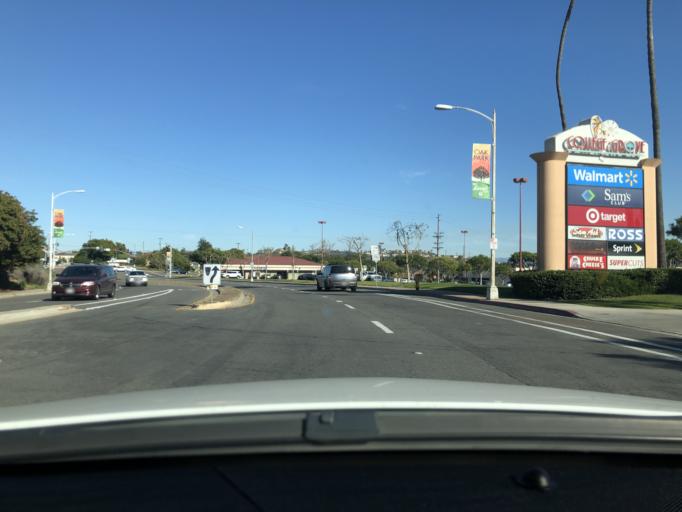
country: US
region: California
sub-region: San Diego County
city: Lemon Grove
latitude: 32.7431
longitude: -117.0551
